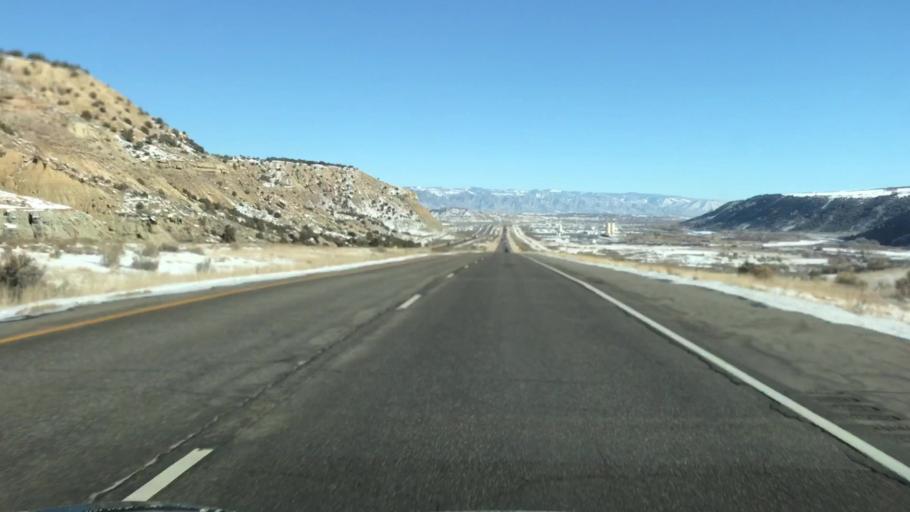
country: US
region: Colorado
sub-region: Garfield County
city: Rifle
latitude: 39.5086
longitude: -107.8793
